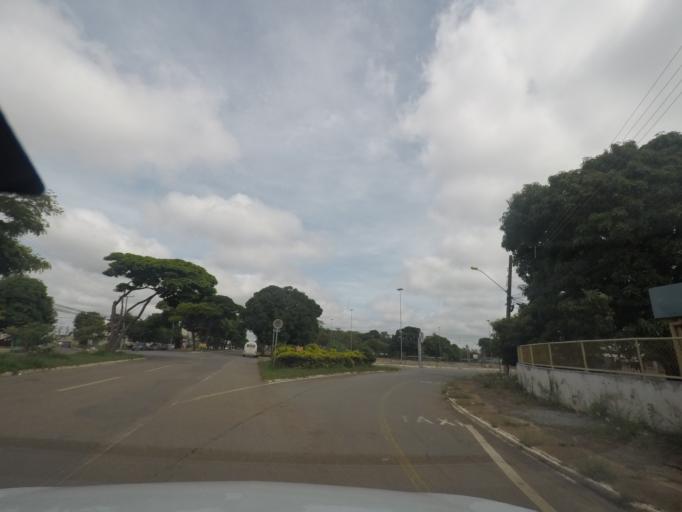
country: BR
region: Goias
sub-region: Goiania
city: Goiania
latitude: -16.6339
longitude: -49.2264
